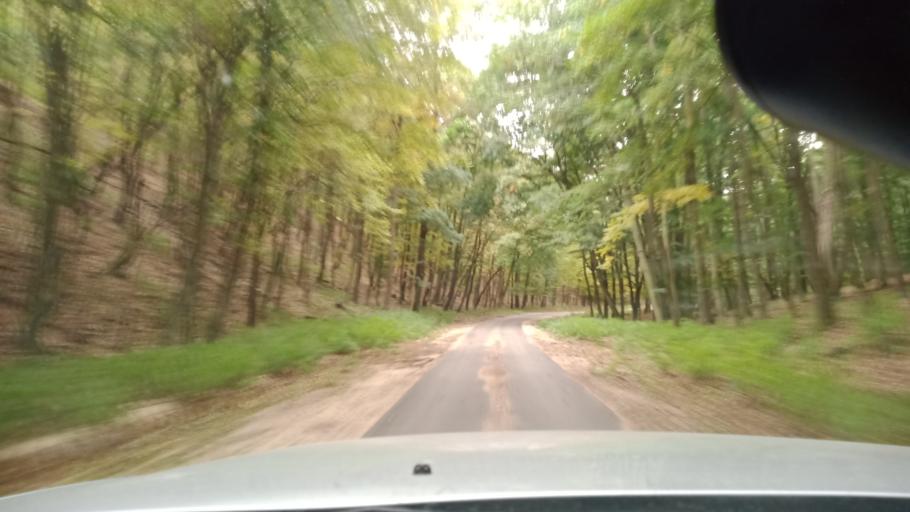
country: HU
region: Komarom-Esztergom
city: Oroszlany
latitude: 47.3866
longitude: 18.3239
